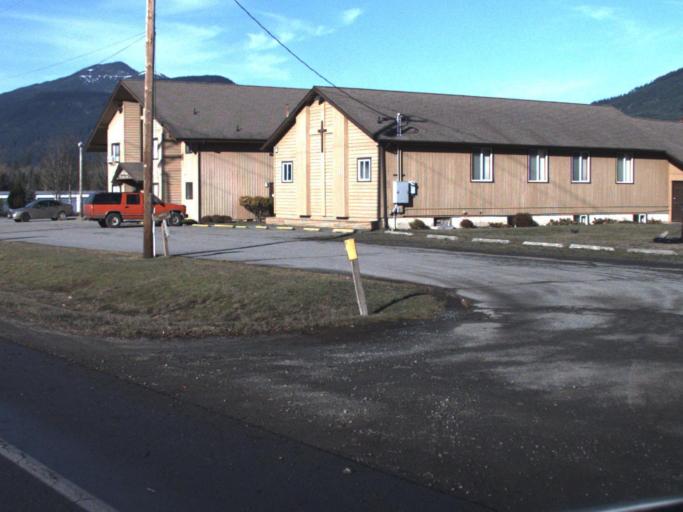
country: US
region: Washington
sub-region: Snohomish County
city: Darrington
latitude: 48.2572
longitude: -121.6131
